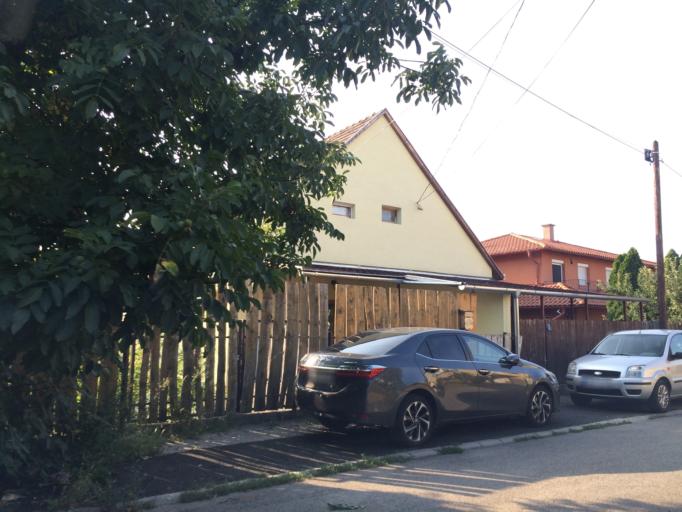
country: HU
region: Pest
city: Szentendre
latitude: 47.6767
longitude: 19.0552
